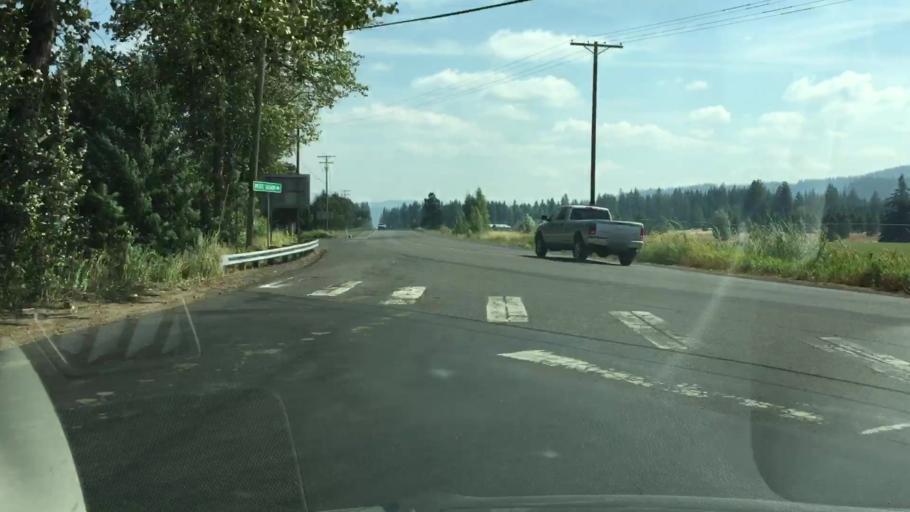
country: US
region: Washington
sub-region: Klickitat County
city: White Salmon
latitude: 45.9963
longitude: -121.5257
